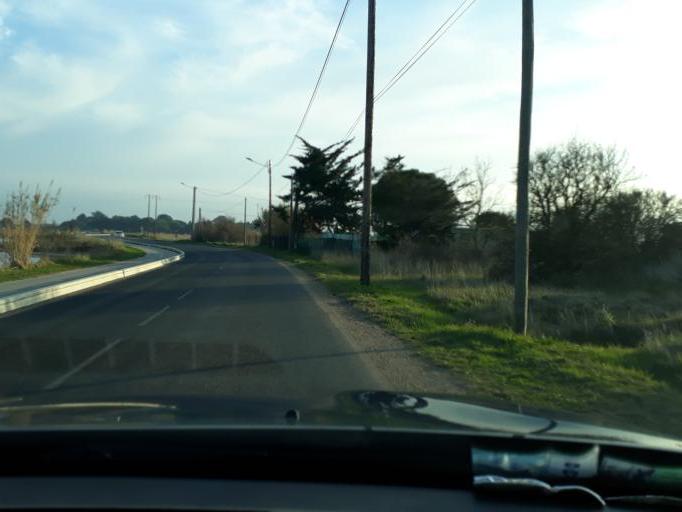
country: FR
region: Languedoc-Roussillon
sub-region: Departement de l'Herault
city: Marseillan
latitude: 43.3269
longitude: 3.5310
